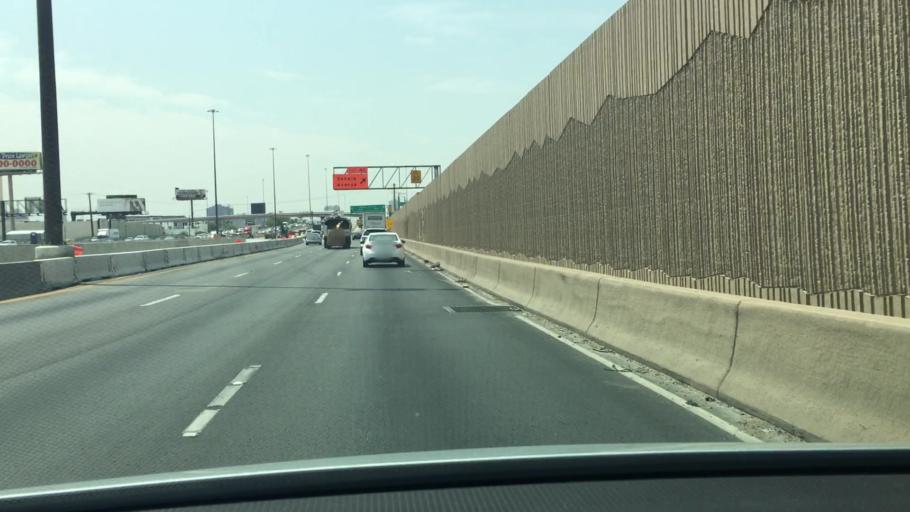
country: US
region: Nevada
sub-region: Clark County
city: Las Vegas
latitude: 36.1504
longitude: -115.1676
